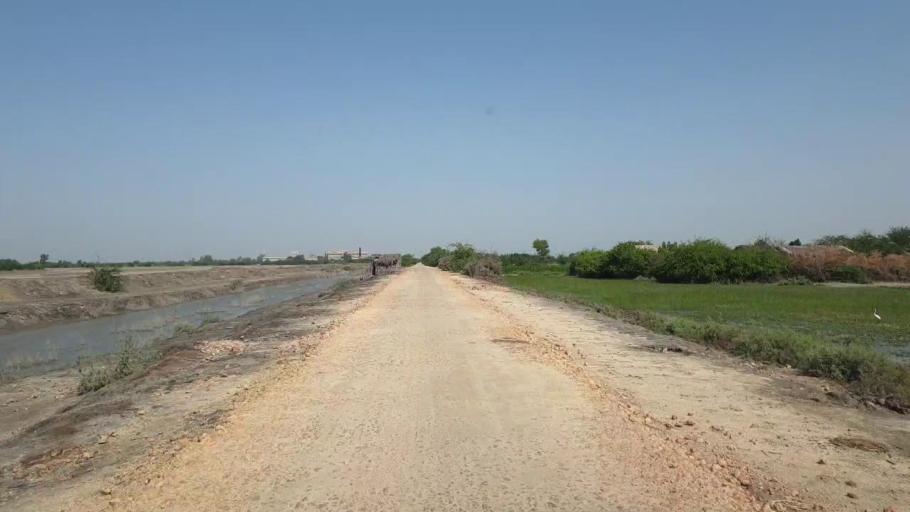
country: PK
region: Sindh
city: Tando Bago
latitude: 24.7324
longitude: 69.0742
